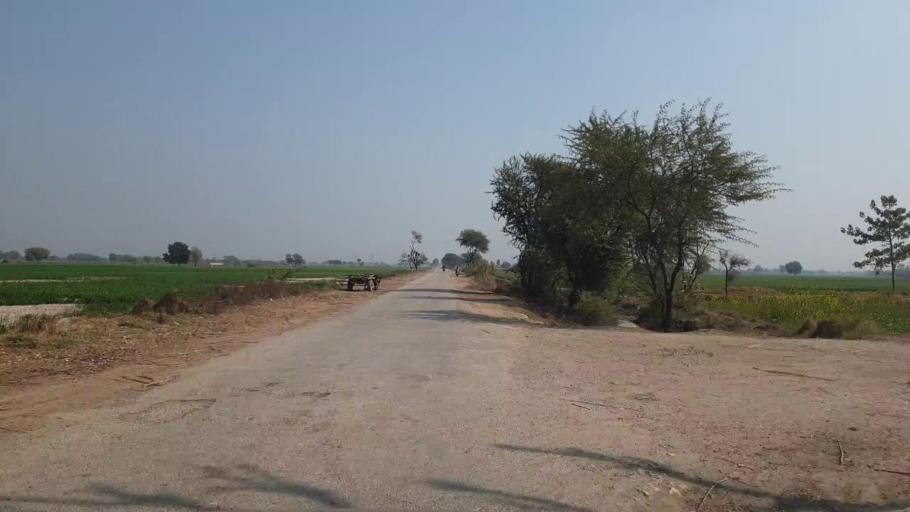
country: PK
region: Sindh
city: Bhit Shah
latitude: 25.7528
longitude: 68.5177
